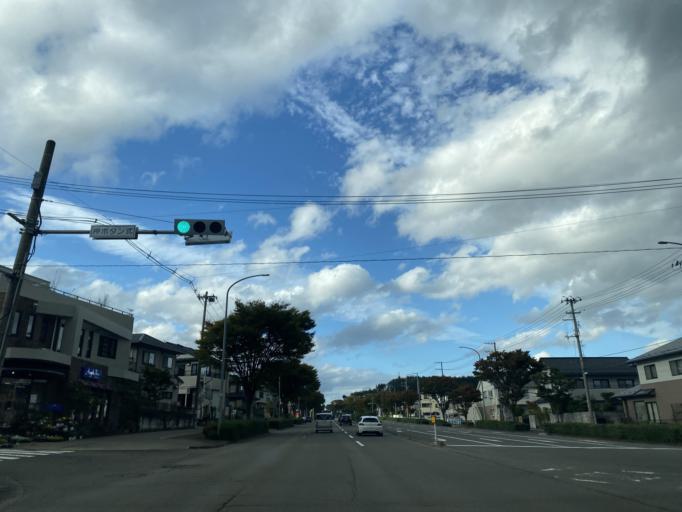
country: JP
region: Miyagi
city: Sendai-shi
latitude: 38.2991
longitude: 140.8541
